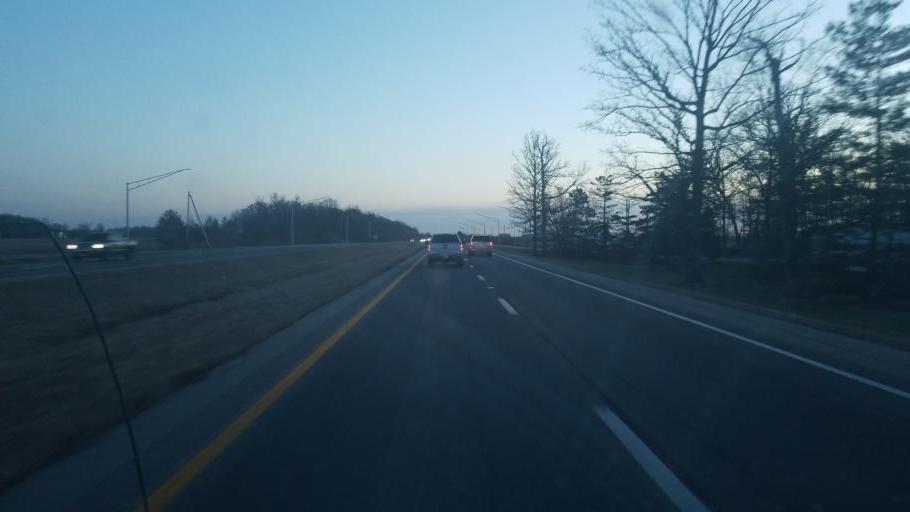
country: US
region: Ohio
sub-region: Marion County
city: Marion
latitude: 40.5269
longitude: -83.0749
